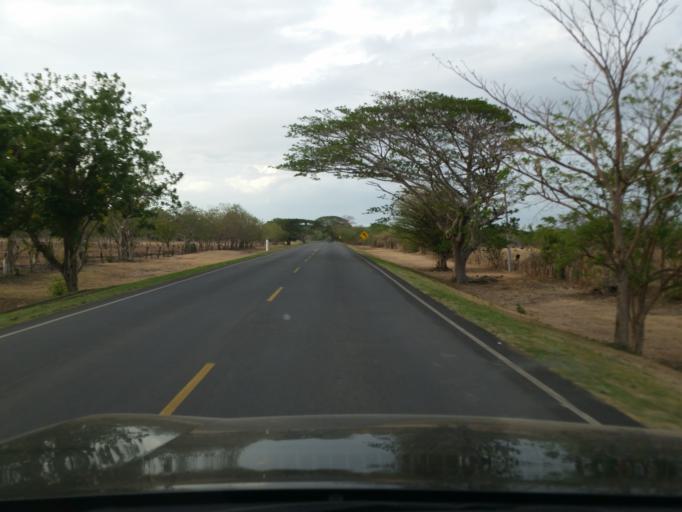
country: NI
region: Rivas
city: Belen
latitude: 11.5750
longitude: -85.8990
